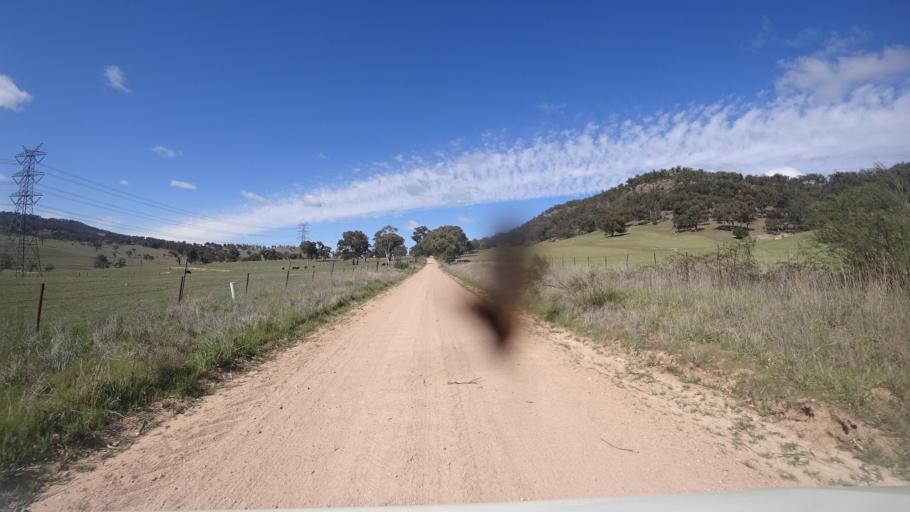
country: AU
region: New South Wales
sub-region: Lithgow
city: Portland
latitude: -33.5268
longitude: 149.9351
